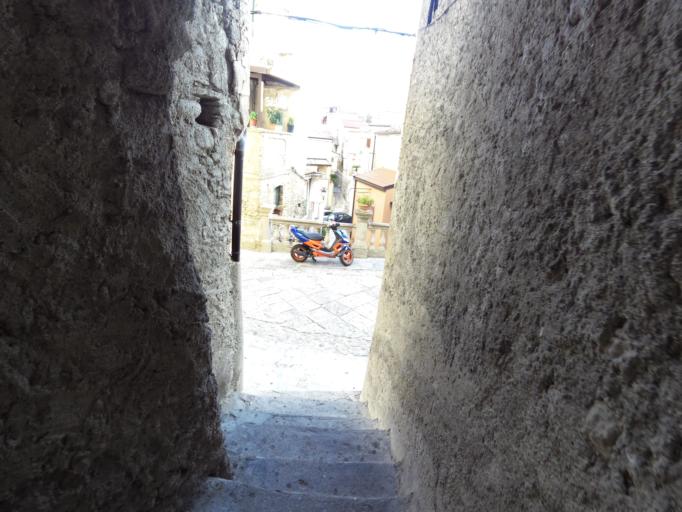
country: IT
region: Calabria
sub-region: Provincia di Reggio Calabria
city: Caulonia
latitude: 38.3823
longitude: 16.4066
